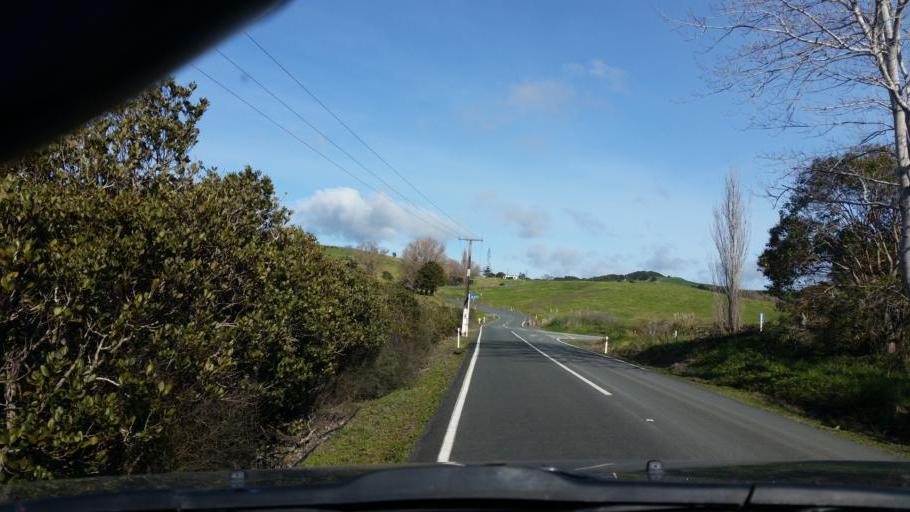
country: NZ
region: Auckland
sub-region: Auckland
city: Wellsford
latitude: -36.1215
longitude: 174.3624
